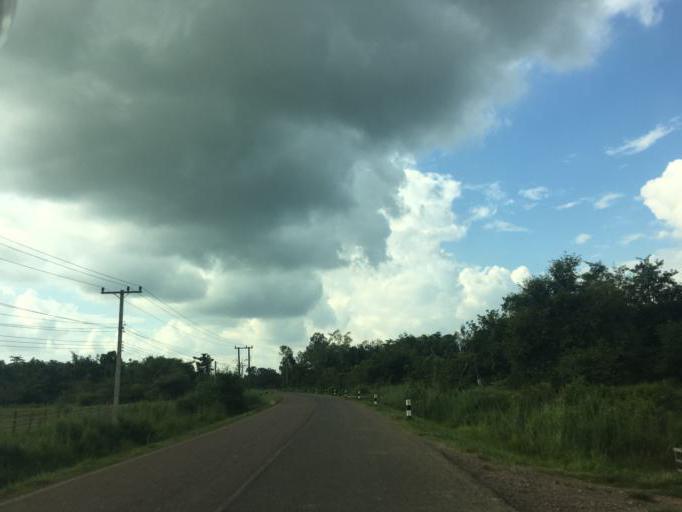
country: TH
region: Nong Khai
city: Sangkhom
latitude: 18.1505
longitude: 102.2714
